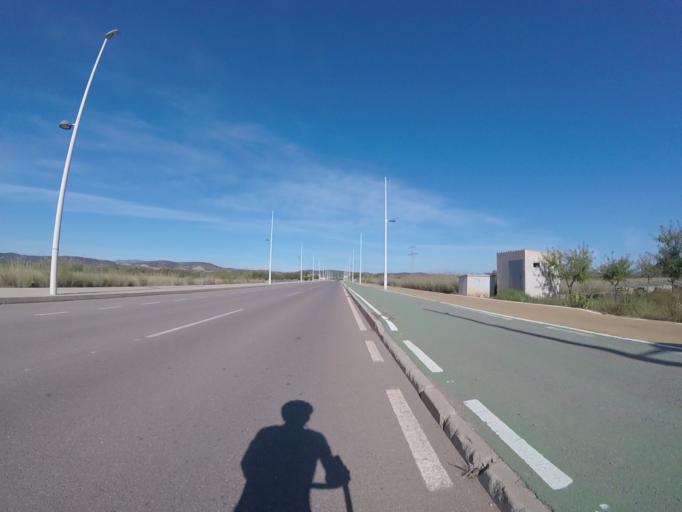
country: ES
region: Valencia
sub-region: Provincia de Castello
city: Torreblanca
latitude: 40.2147
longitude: 0.2218
